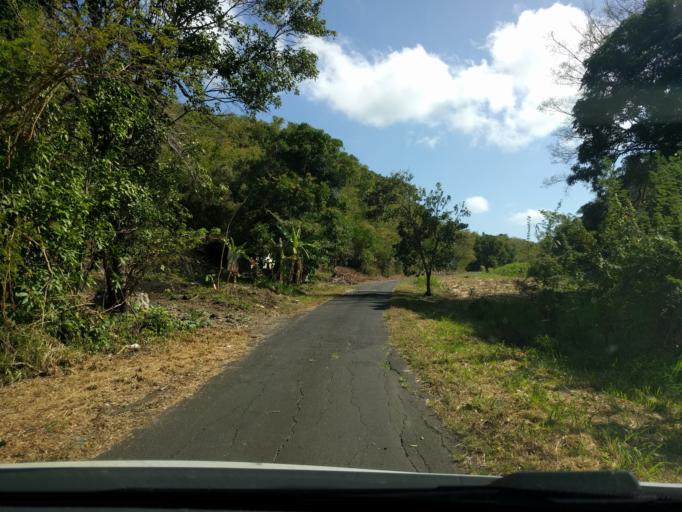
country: GP
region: Guadeloupe
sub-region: Guadeloupe
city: Grand-Bourg
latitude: 15.9721
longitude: -61.2624
